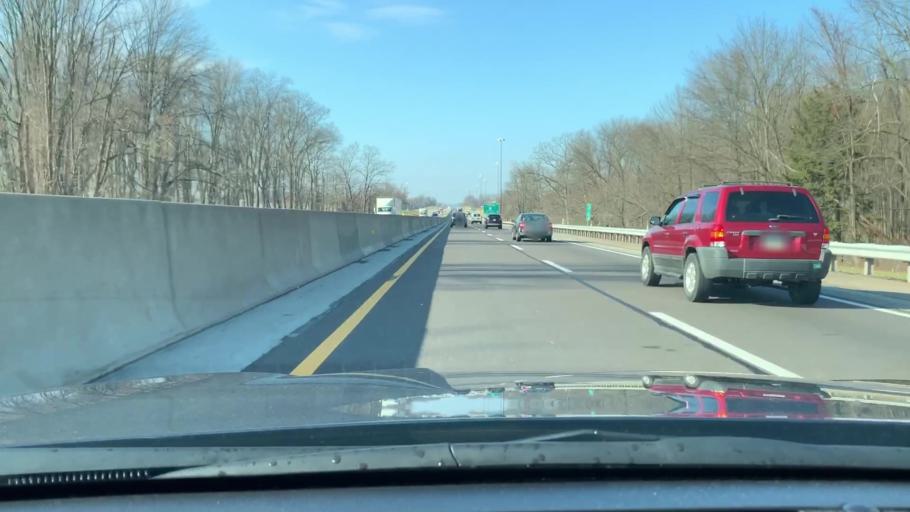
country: US
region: Pennsylvania
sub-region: Chester County
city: Chester Springs
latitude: 40.0659
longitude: -75.6575
